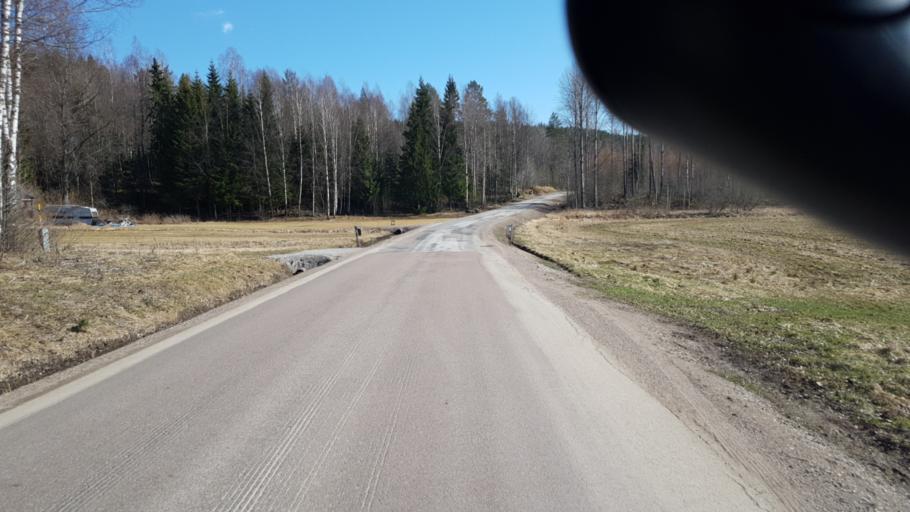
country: SE
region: Vaermland
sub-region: Arvika Kommun
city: Arvika
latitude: 59.6551
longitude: 12.8050
